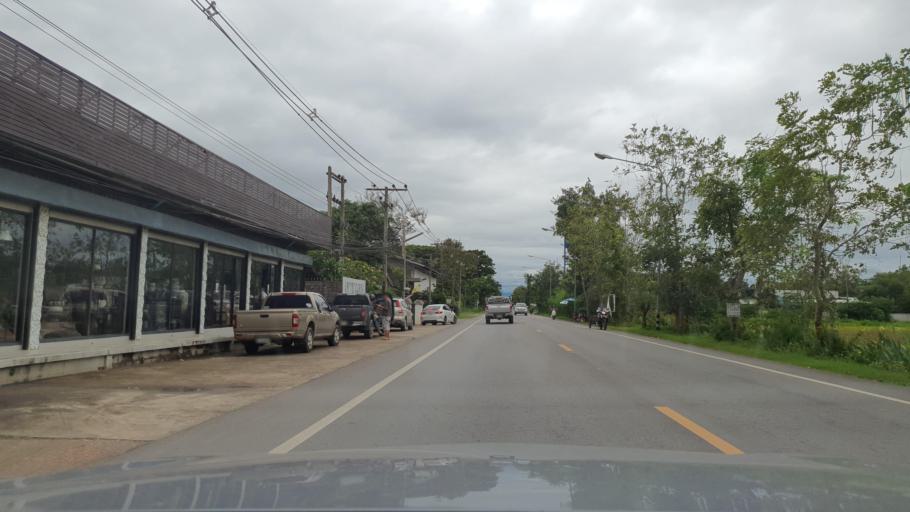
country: TH
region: Lamphun
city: Lamphun
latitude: 18.5873
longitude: 98.9868
